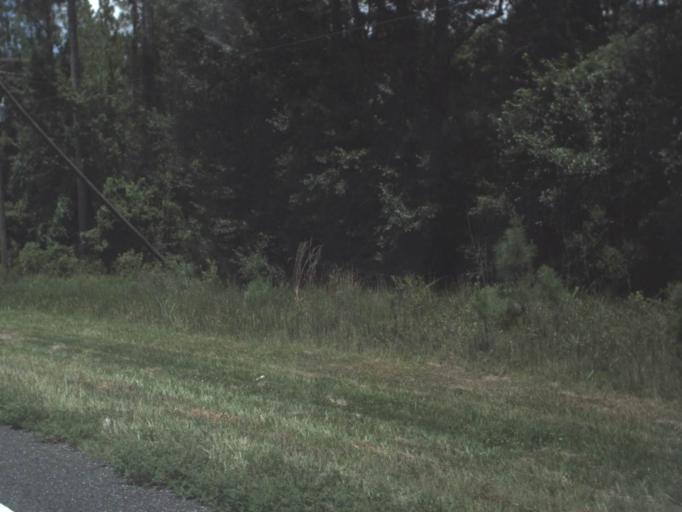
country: US
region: Florida
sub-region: Taylor County
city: Perry
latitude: 29.9735
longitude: -83.4824
